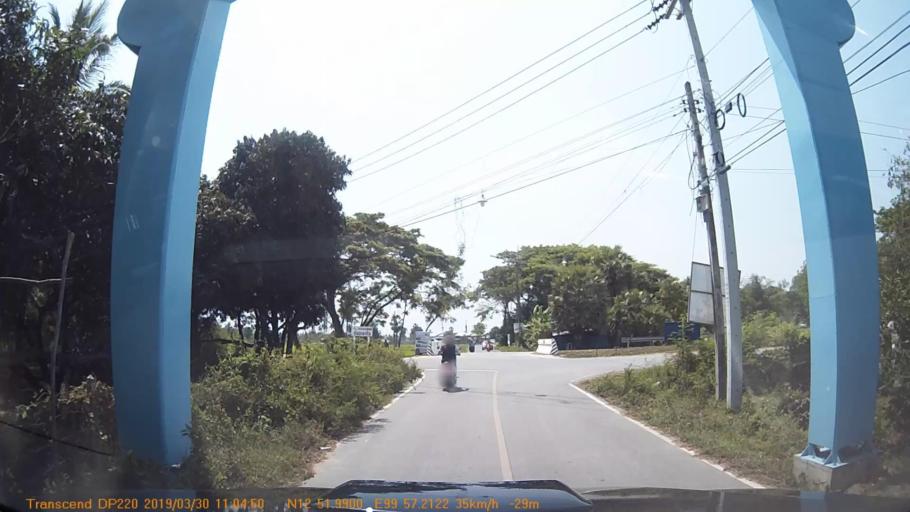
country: TH
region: Phetchaburi
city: Cha-am
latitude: 12.8664
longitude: 99.9536
